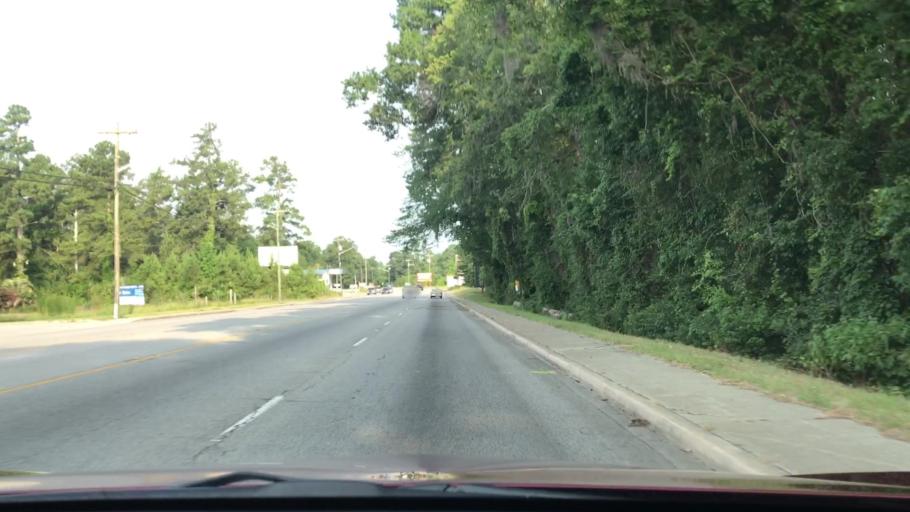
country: US
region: South Carolina
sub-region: Orangeburg County
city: Edisto
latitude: 33.4817
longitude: -80.8834
